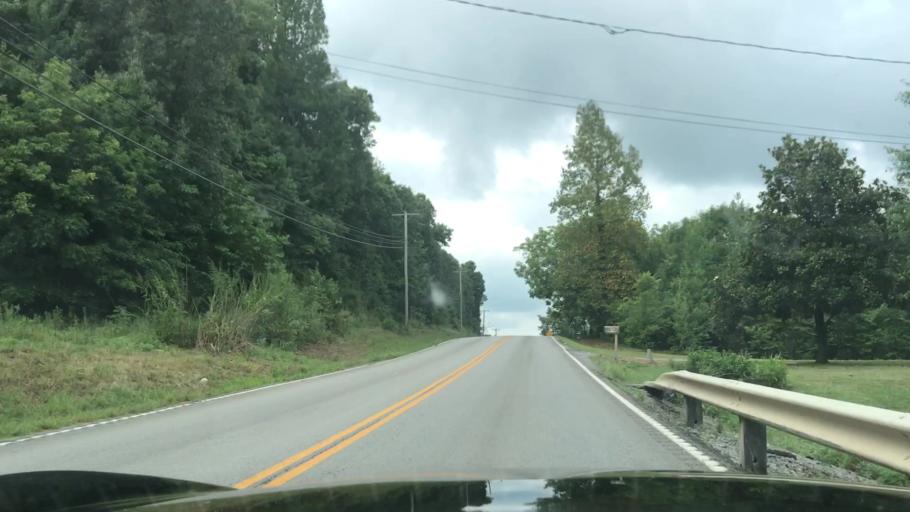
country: US
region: Kentucky
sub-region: Muhlenberg County
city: Central City
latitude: 37.2128
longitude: -87.0639
